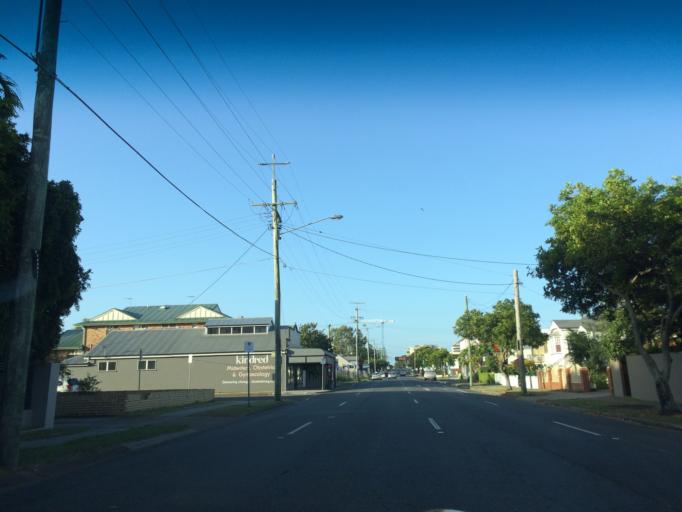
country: AU
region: Queensland
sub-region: Brisbane
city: Woolloongabba
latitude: -27.4840
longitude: 153.0404
